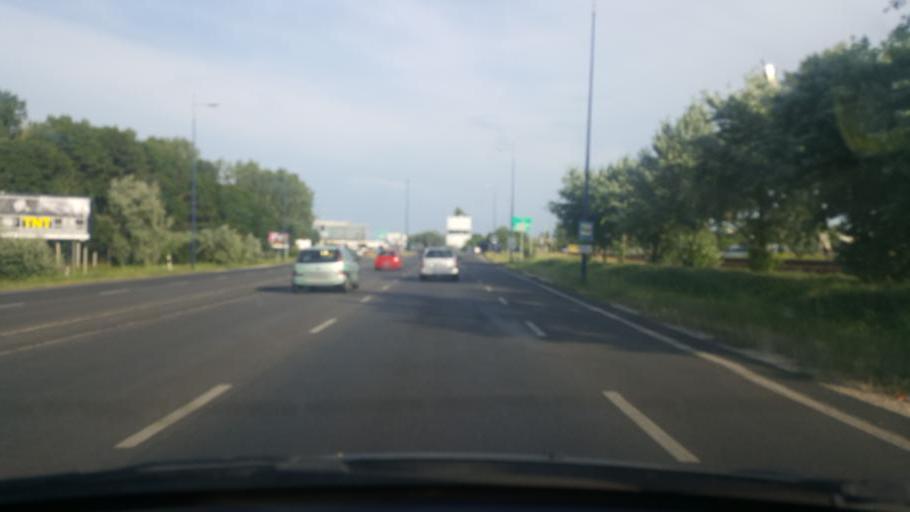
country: HU
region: Pest
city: Gyal
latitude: 47.4220
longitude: 19.2415
